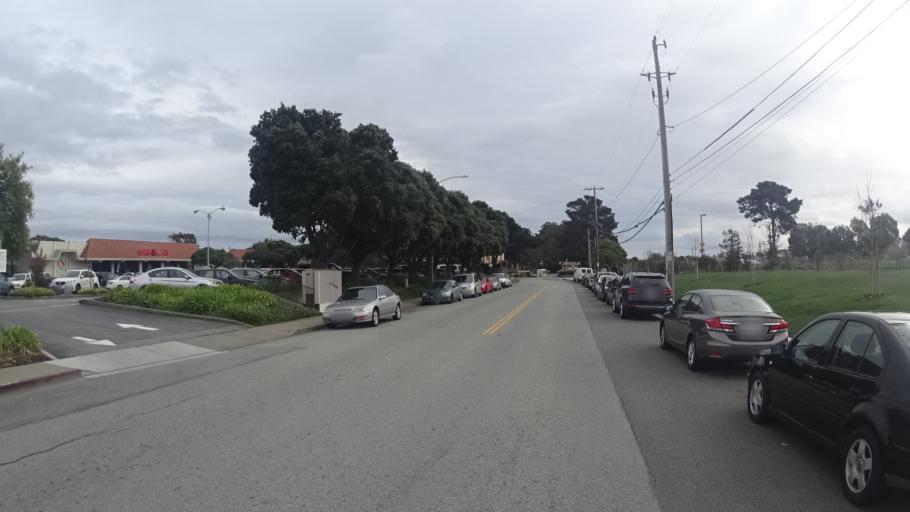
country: US
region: California
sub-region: San Mateo County
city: South San Francisco
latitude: 37.6553
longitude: -122.4329
